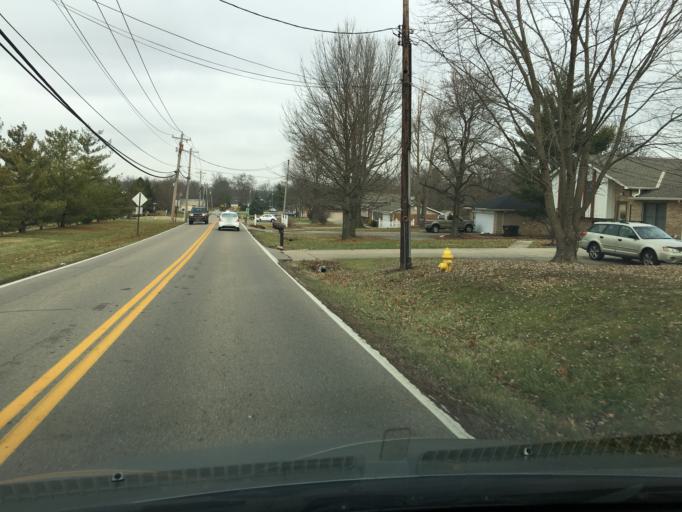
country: US
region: Ohio
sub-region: Hamilton County
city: Sharonville
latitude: 39.3135
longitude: -84.3997
